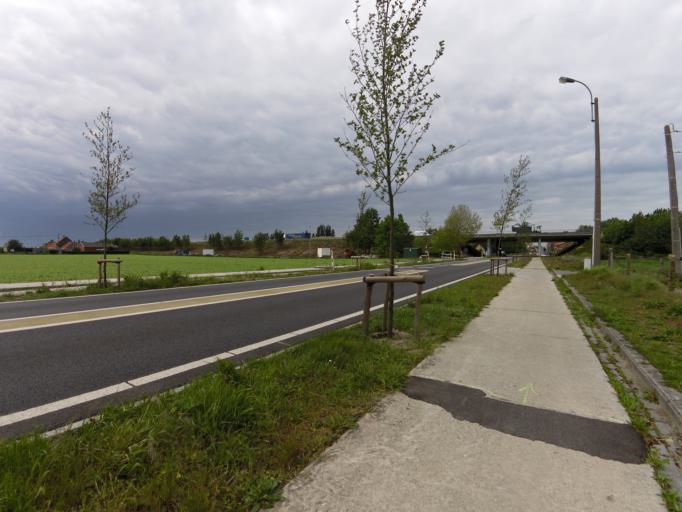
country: BE
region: Flanders
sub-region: Provincie West-Vlaanderen
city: Oudenburg
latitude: 51.1741
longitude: 3.0087
